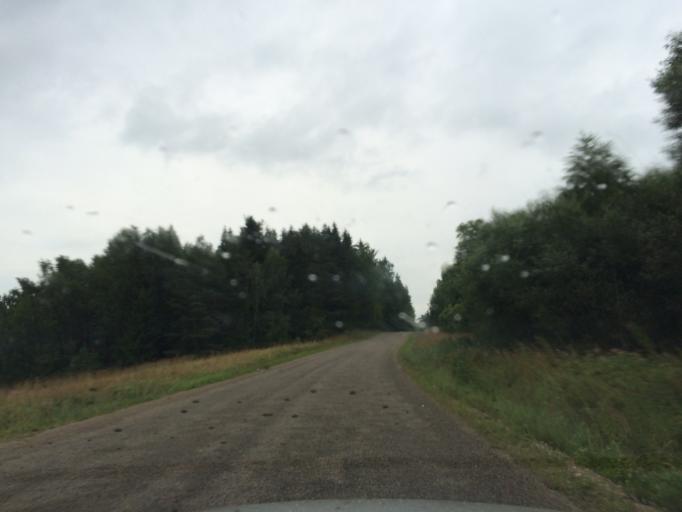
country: LV
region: Rezekne
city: Rezekne
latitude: 56.5660
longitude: 27.4551
